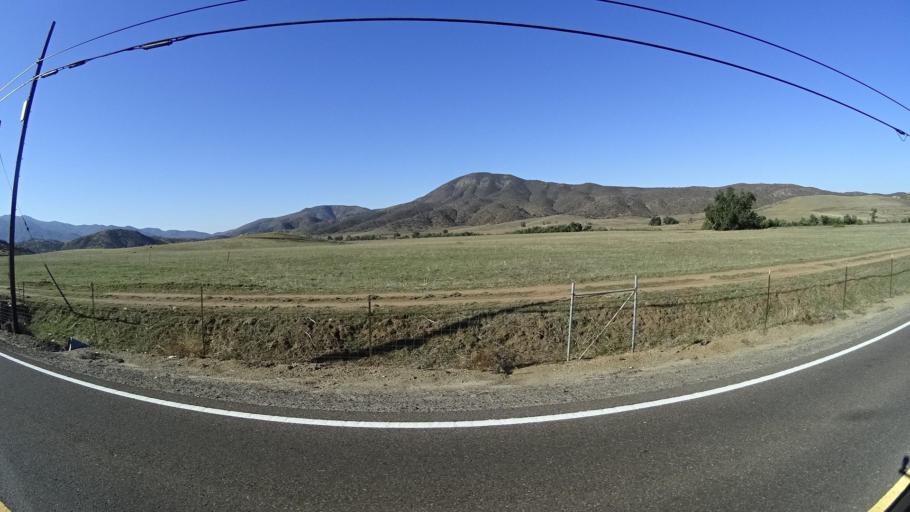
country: US
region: California
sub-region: San Diego County
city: Jamul
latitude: 32.6938
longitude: -116.8574
